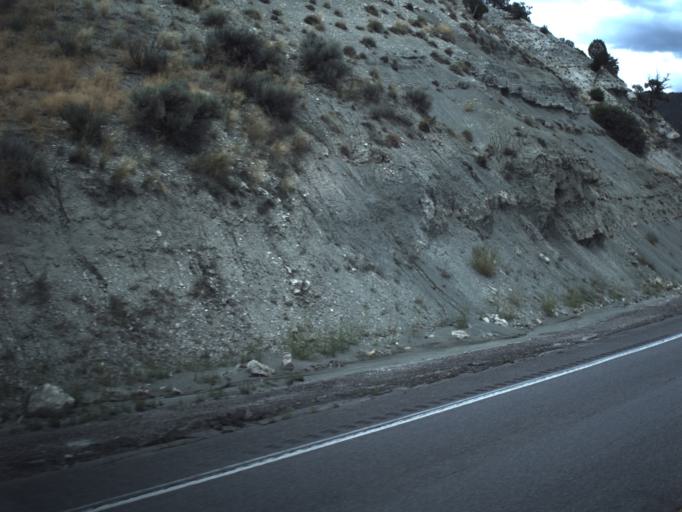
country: US
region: Utah
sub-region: Utah County
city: Mapleton
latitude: 39.9652
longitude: -111.3176
